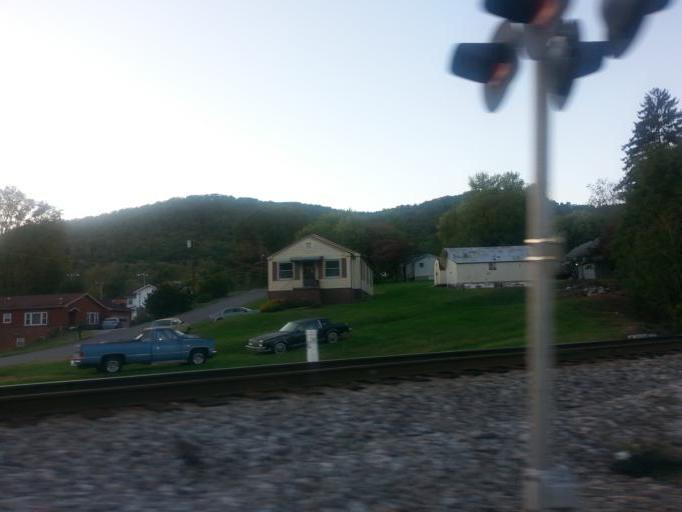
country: US
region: Tennessee
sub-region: Campbell County
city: LaFollette
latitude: 36.3740
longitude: -84.1311
